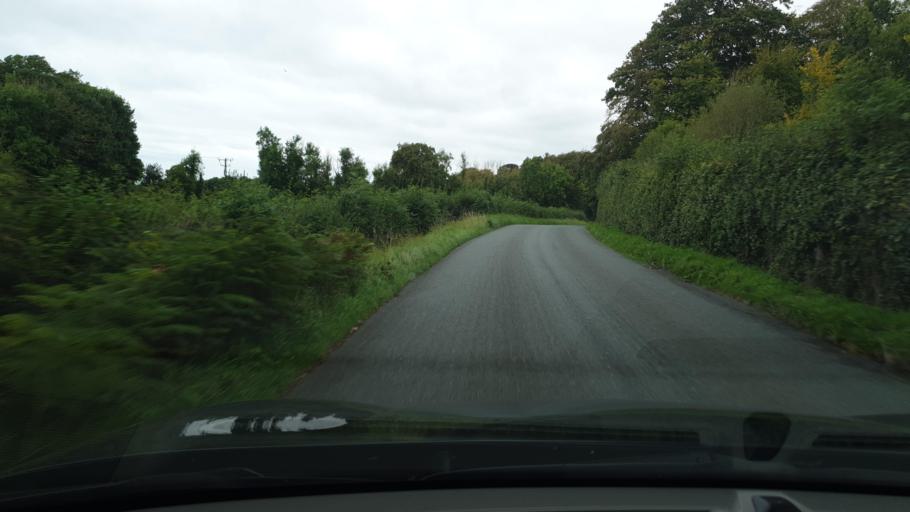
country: IE
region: Leinster
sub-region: Kildare
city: Kilcock
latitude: 53.3989
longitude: -6.6409
